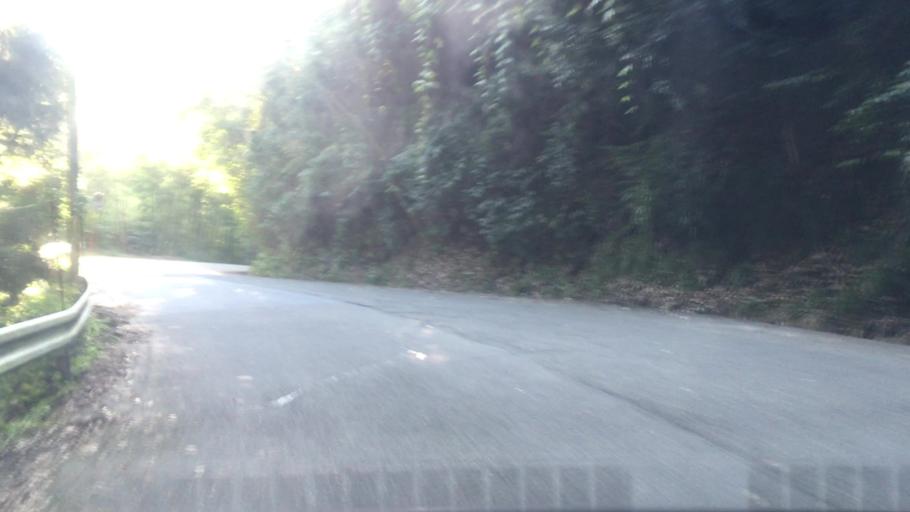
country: JP
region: Hyogo
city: Toyooka
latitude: 35.6125
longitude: 134.8343
